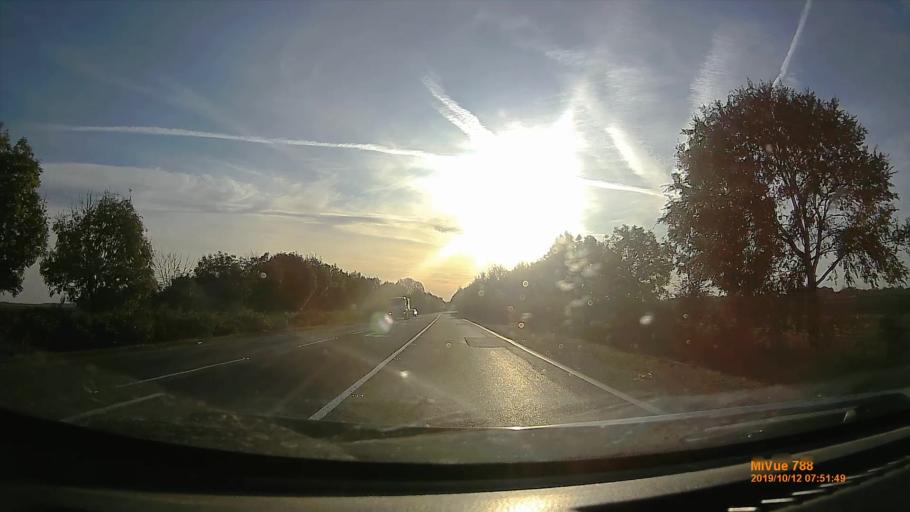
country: HU
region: Hajdu-Bihar
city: Biharkeresztes
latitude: 47.1394
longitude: 21.7310
